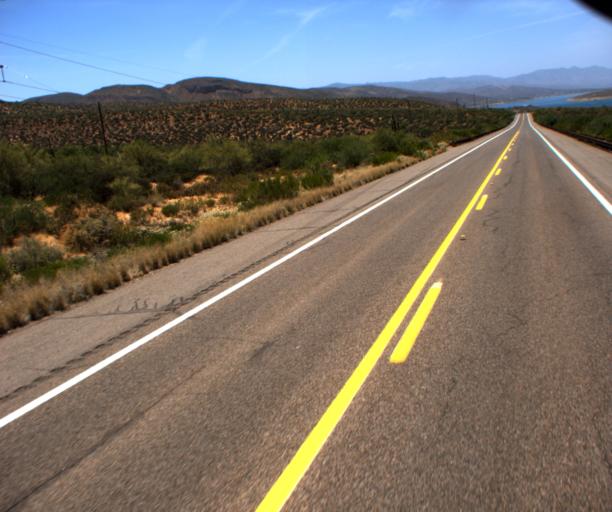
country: US
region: Arizona
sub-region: Gila County
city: Tonto Basin
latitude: 33.6567
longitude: -111.1096
